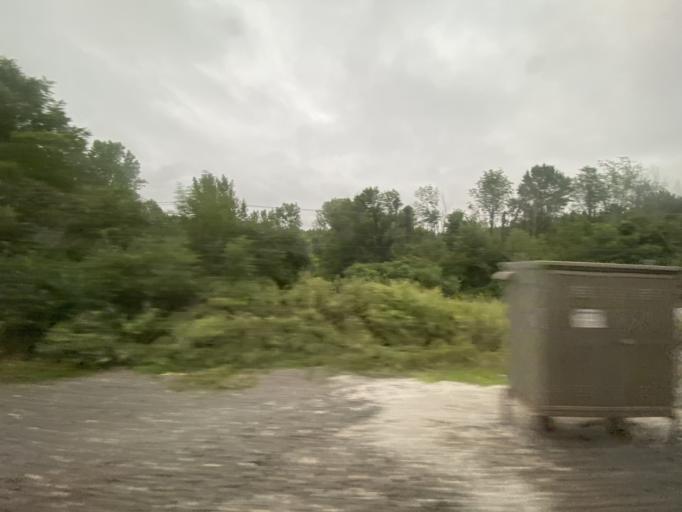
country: US
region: Indiana
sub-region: LaPorte County
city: Westville
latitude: 41.5986
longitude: -86.9147
